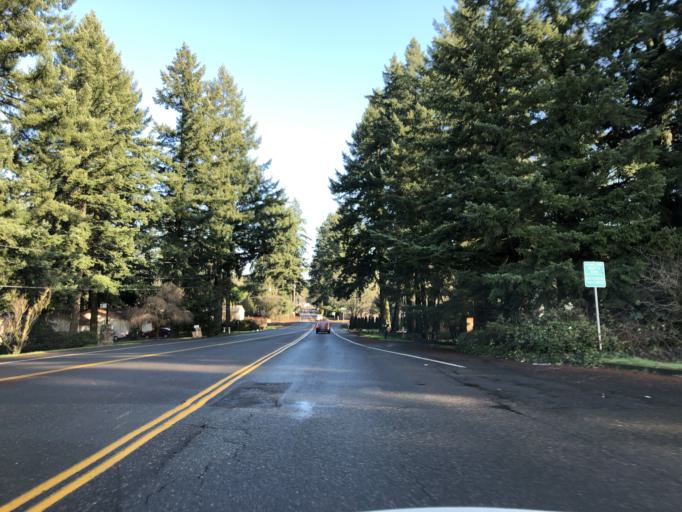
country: US
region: Oregon
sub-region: Washington County
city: Durham
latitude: 45.4087
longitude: -122.7424
